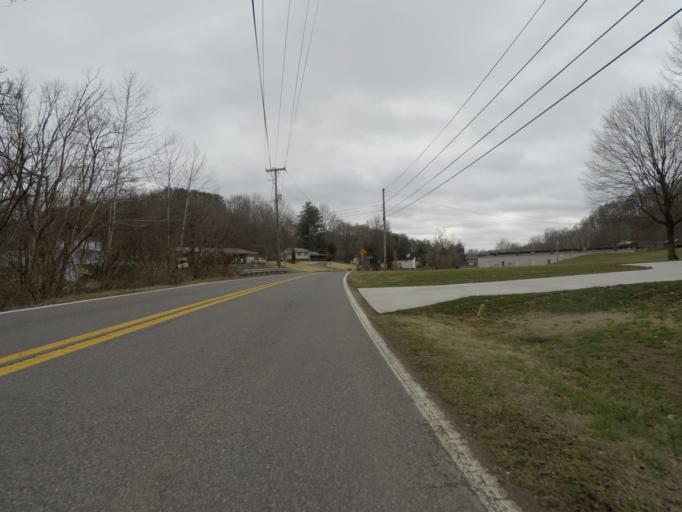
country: US
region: West Virginia
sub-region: Cabell County
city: Barboursville
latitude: 38.4286
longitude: -82.2922
